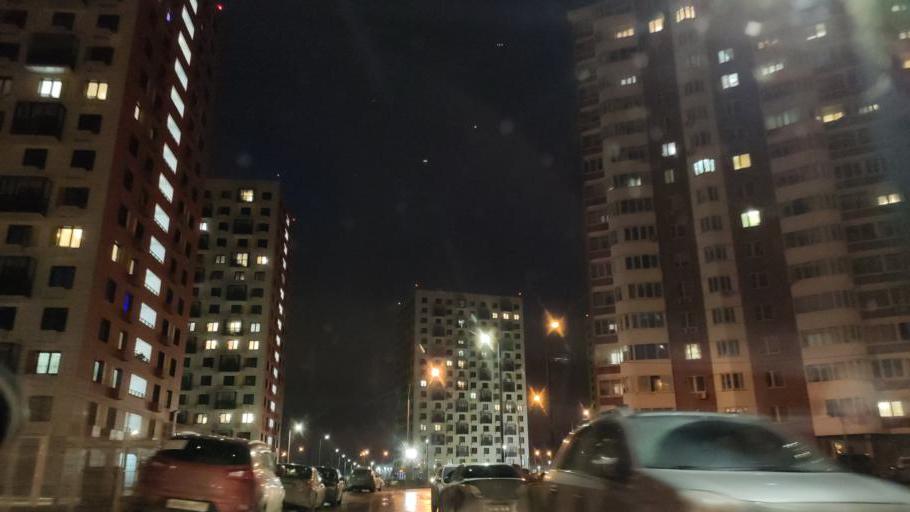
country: RU
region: Moscow
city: Annino
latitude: 55.5293
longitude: 37.6159
